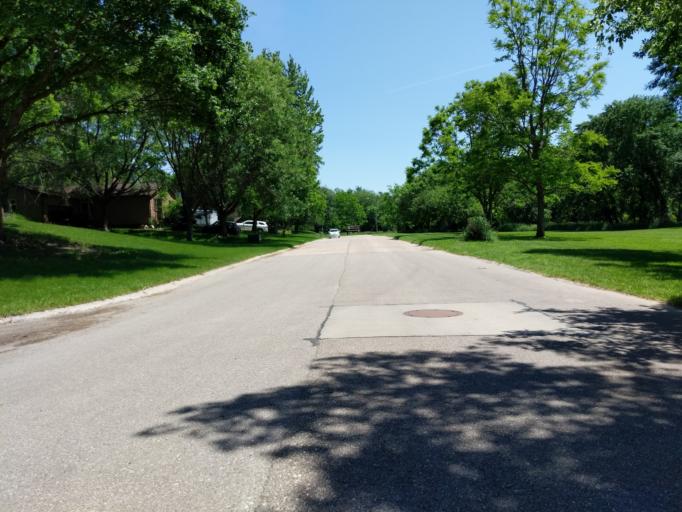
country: US
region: Iowa
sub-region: Linn County
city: Cedar Rapids
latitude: 42.0170
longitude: -91.6258
